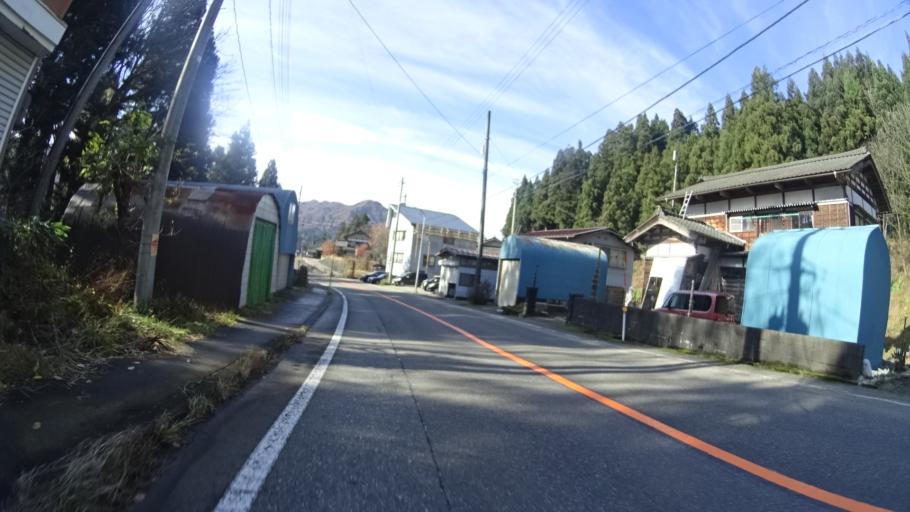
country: JP
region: Niigata
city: Muikamachi
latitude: 37.2127
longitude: 139.0535
